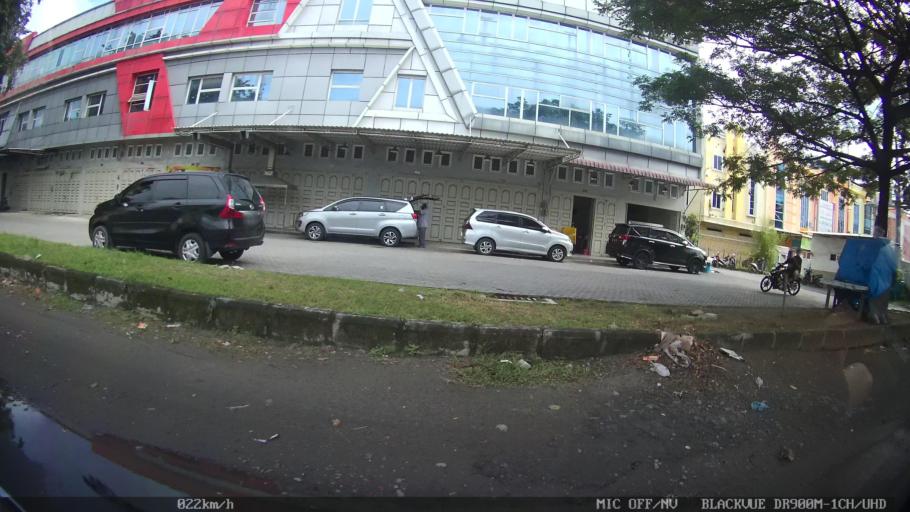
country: ID
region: North Sumatra
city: Medan
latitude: 3.6287
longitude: 98.7012
